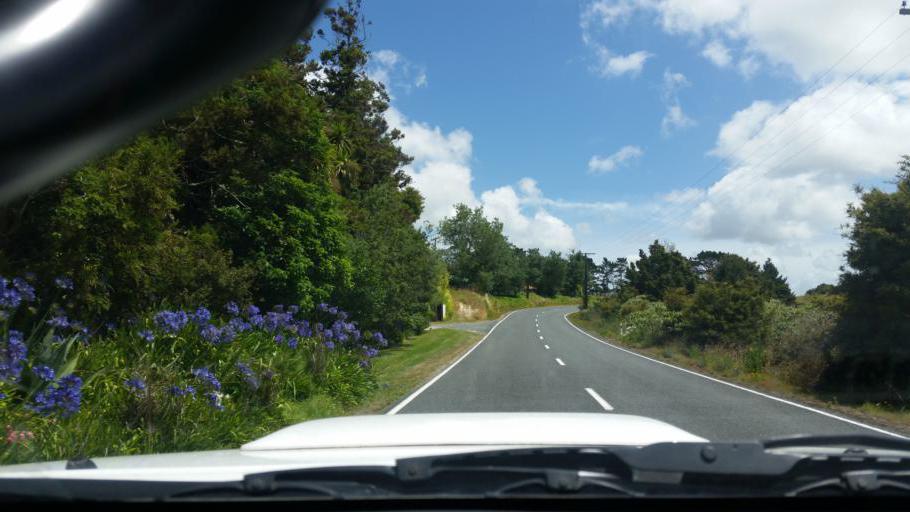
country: NZ
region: Northland
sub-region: Whangarei
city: Ruakaka
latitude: -36.0754
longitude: 174.2592
